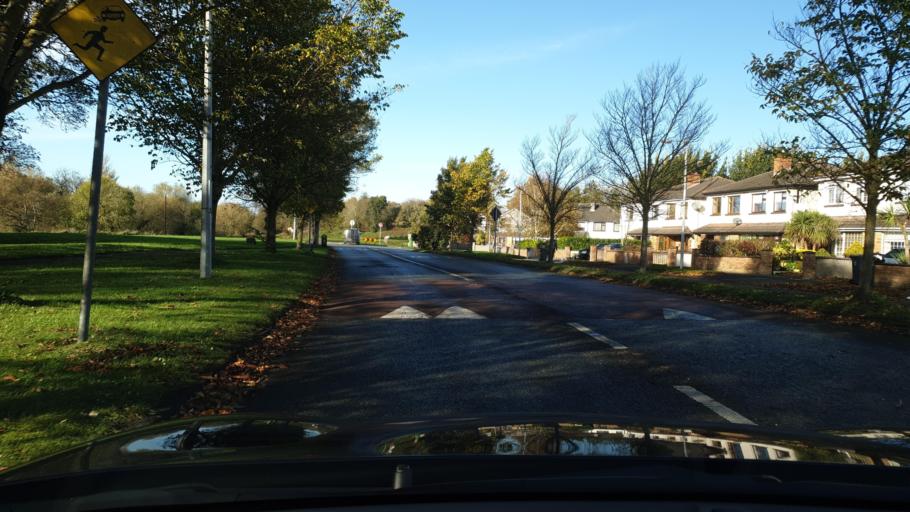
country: IE
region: Leinster
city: Lucan
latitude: 53.3497
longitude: -6.4389
